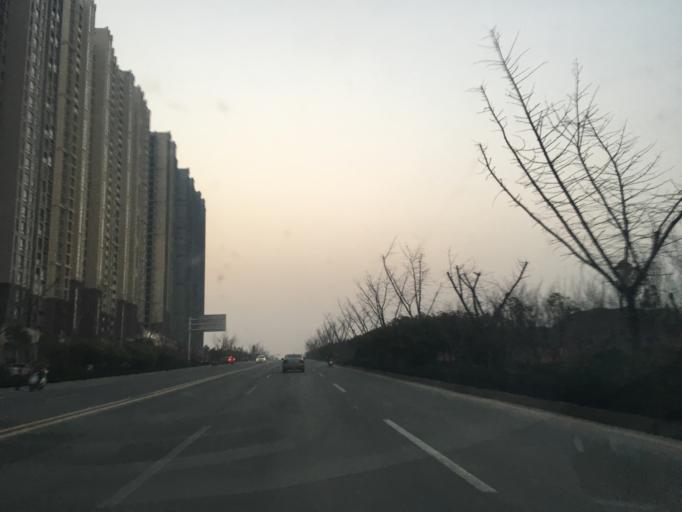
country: CN
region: Hubei
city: Nanhu
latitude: 31.1599
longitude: 115.0104
